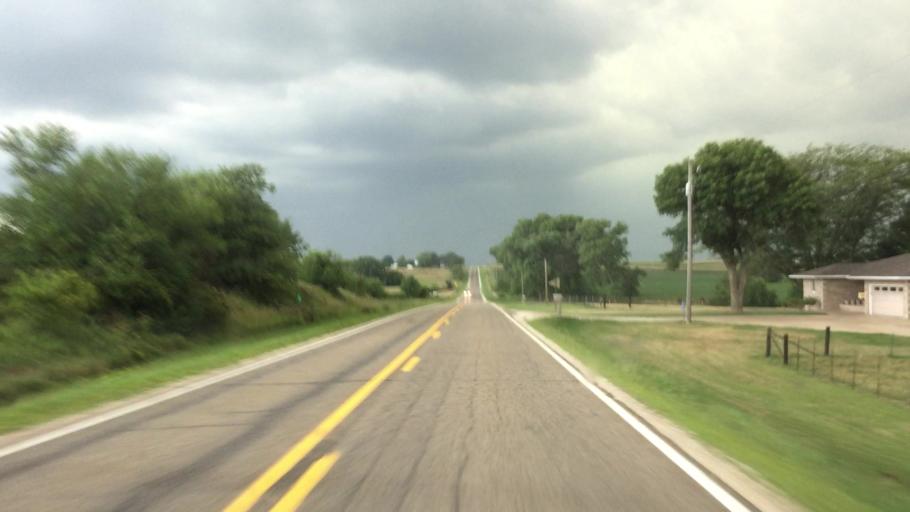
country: US
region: Iowa
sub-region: Henry County
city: Mount Pleasant
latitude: 40.7844
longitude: -91.5359
